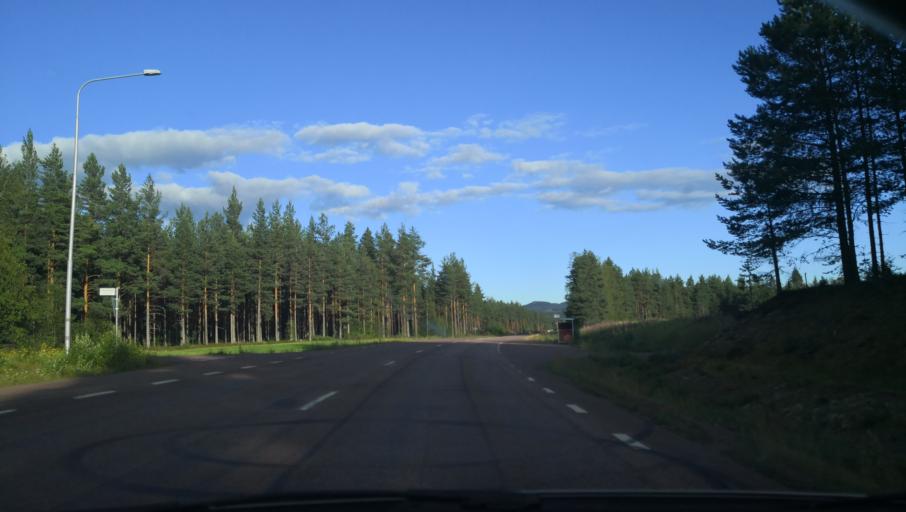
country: SE
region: Dalarna
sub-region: Alvdalens Kommun
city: AElvdalen
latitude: 61.2674
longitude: 14.0081
